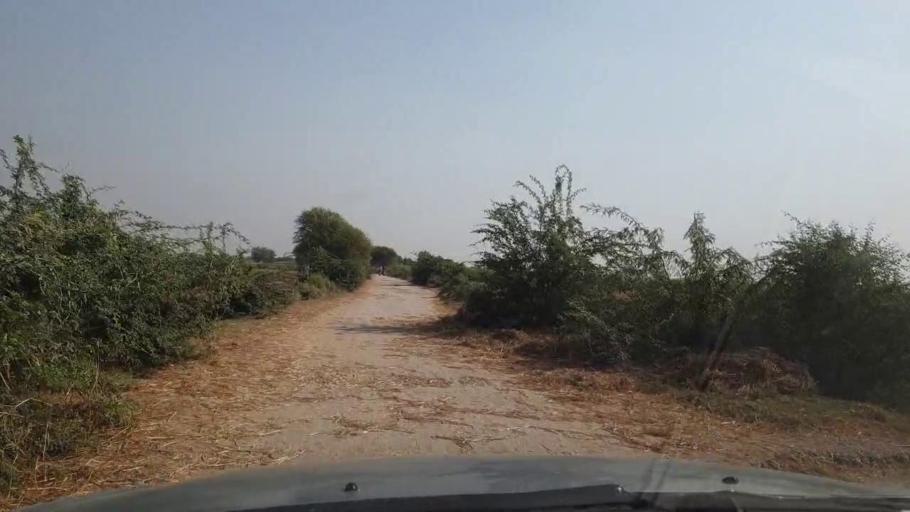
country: PK
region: Sindh
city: Bulri
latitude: 24.9206
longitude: 68.3539
